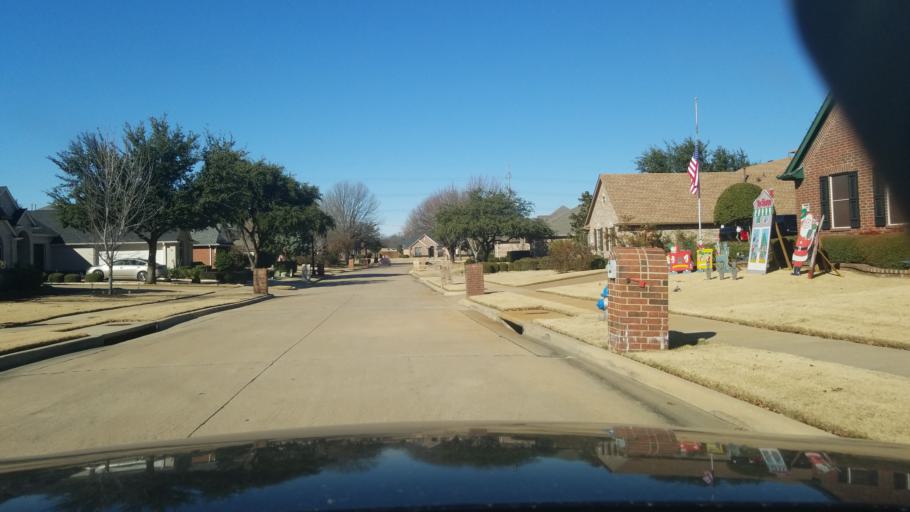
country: US
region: Texas
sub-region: Denton County
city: Corinth
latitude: 33.1609
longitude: -97.0814
